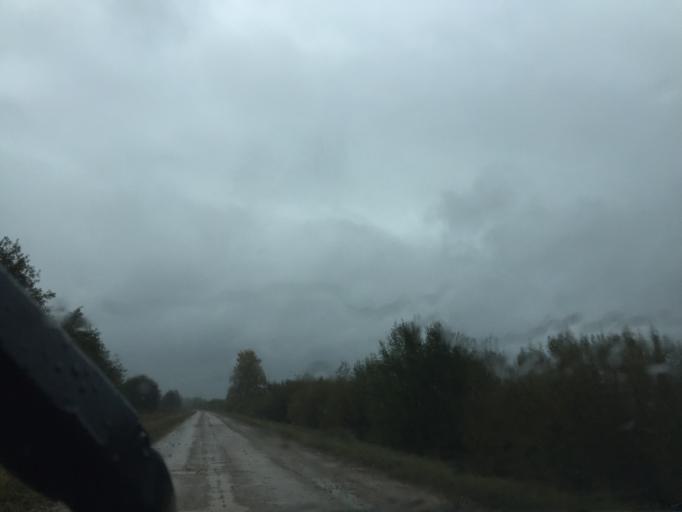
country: LV
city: Tireli
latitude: 56.7388
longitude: 23.5141
